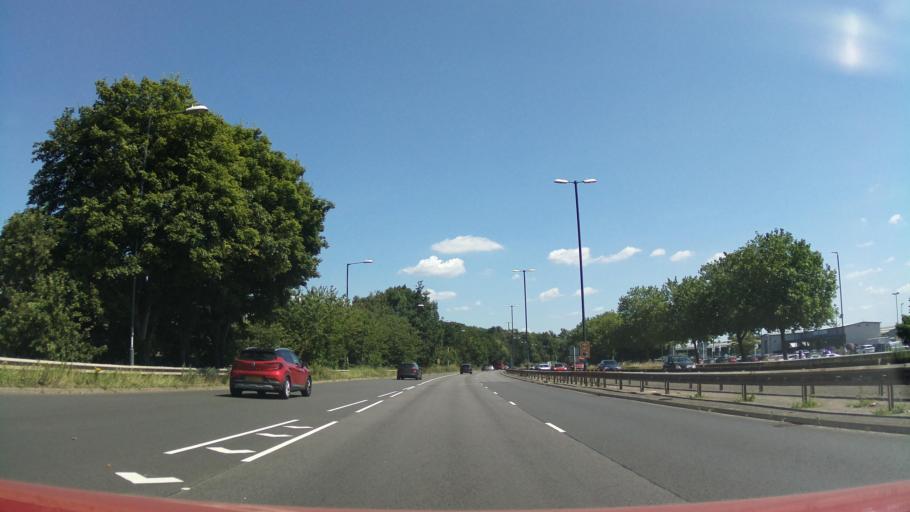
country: GB
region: England
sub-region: Derby
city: Derby
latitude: 52.9242
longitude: -1.4571
